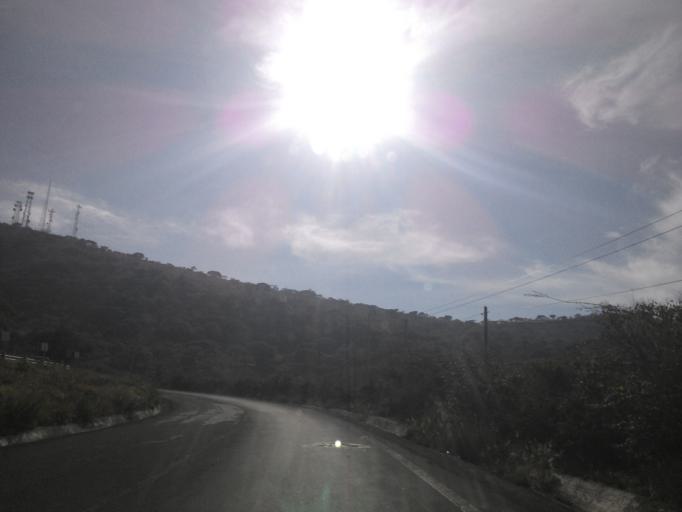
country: MX
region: Jalisco
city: Ixtlahuacan de los Membrillos
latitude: 20.3389
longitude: -103.1864
